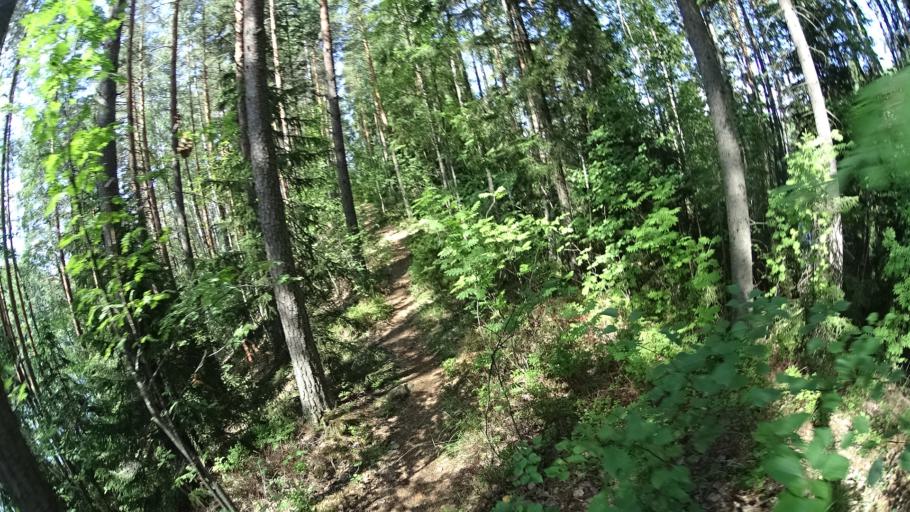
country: FI
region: Haeme
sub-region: Forssa
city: Tammela
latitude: 60.7718
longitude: 23.8554
